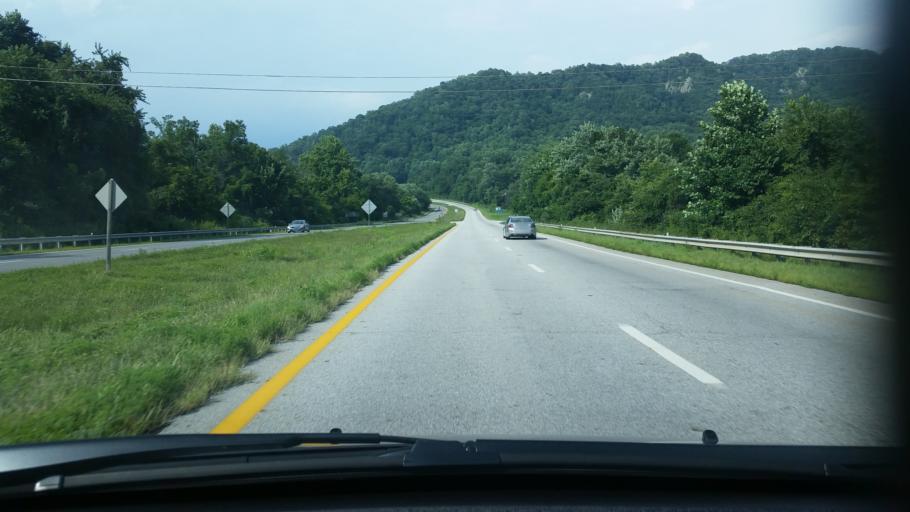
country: US
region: Virginia
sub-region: Nelson County
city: Lovingston
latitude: 37.7623
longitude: -78.8725
